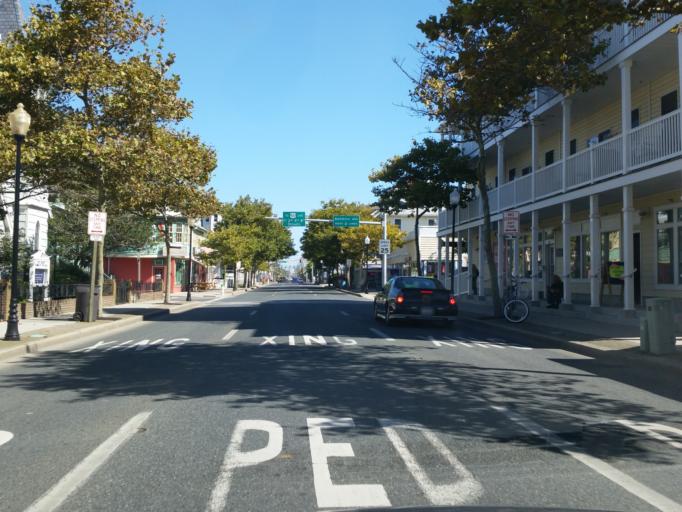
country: US
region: Maryland
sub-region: Worcester County
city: Ocean City
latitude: 38.3300
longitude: -75.0869
